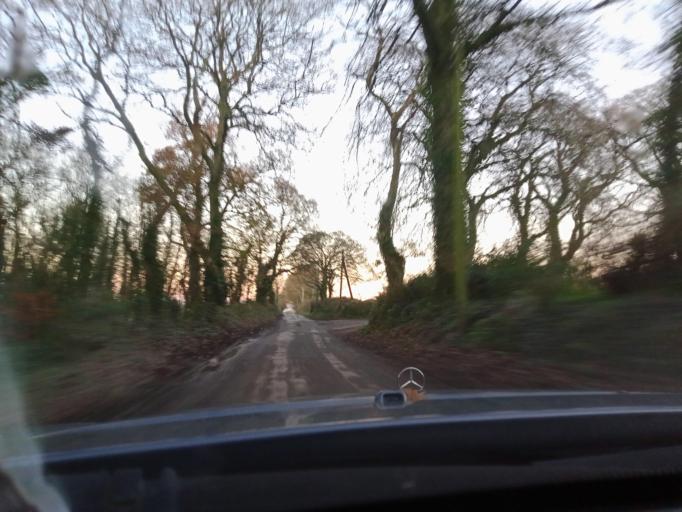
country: IE
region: Leinster
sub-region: Kilkenny
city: Thomastown
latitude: 52.4632
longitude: -7.1011
